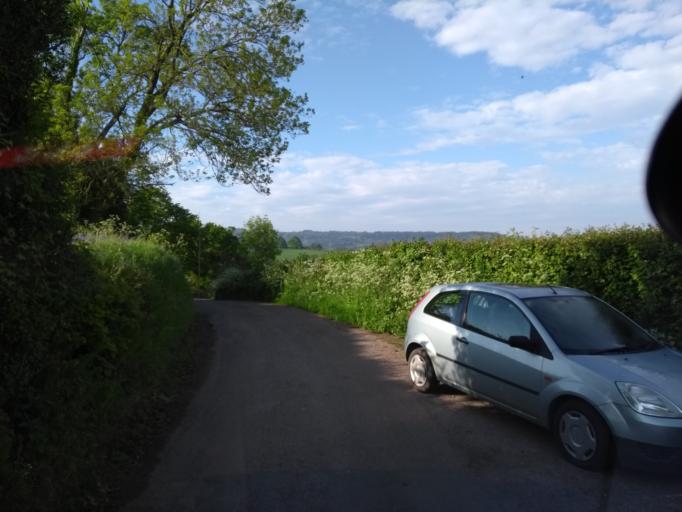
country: GB
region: England
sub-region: Devon
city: Axminster
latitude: 50.7991
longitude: -2.9422
